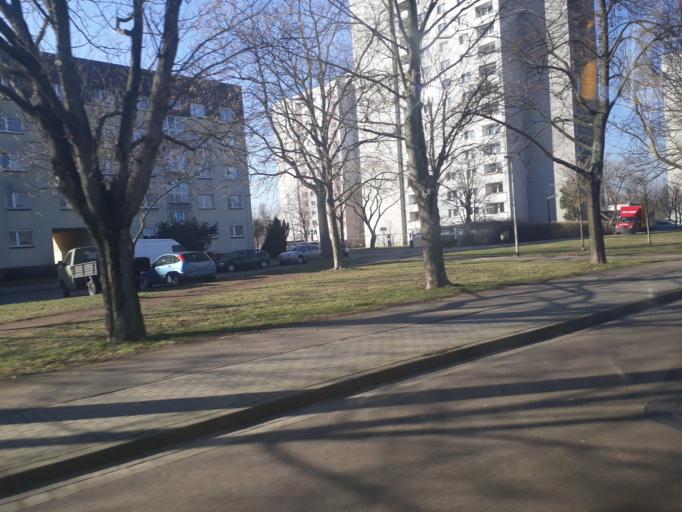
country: DE
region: Saxony
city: Heidenau
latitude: 51.0137
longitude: 13.8198
